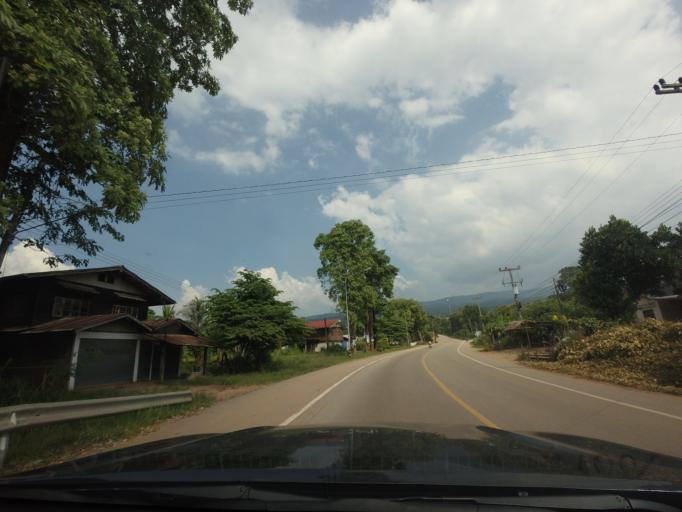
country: TH
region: Phitsanulok
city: Nakhon Thai
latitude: 17.0204
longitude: 100.9246
